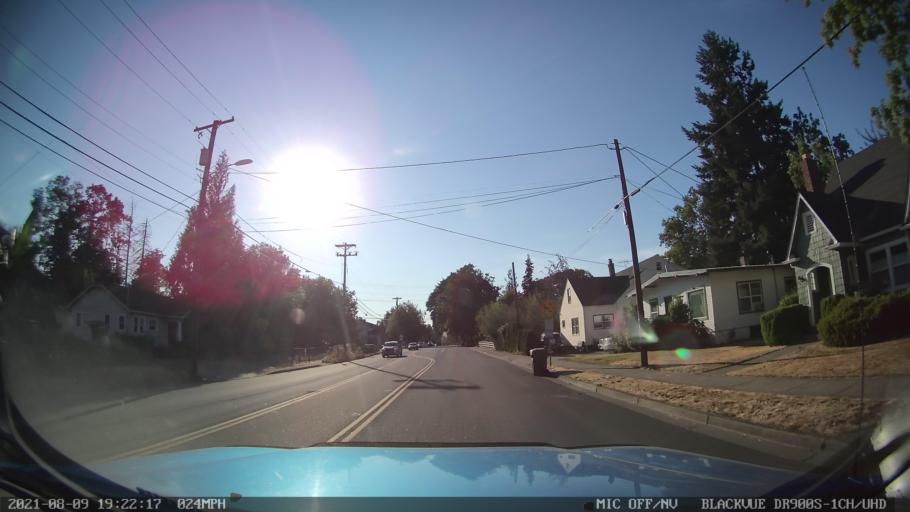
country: US
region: Oregon
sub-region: Marion County
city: Salem
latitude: 44.9393
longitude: -123.0214
